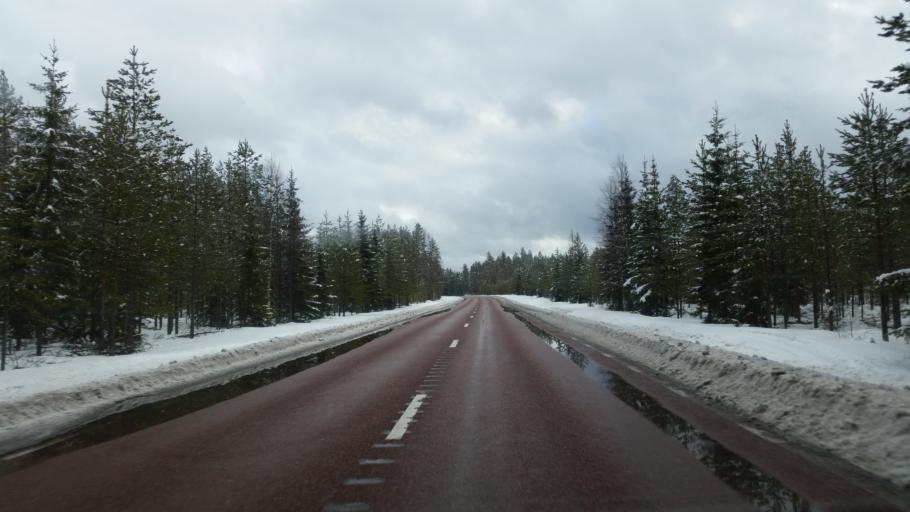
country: SE
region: Gaevleborg
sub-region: Ljusdals Kommun
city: Farila
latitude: 61.9219
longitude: 15.6053
